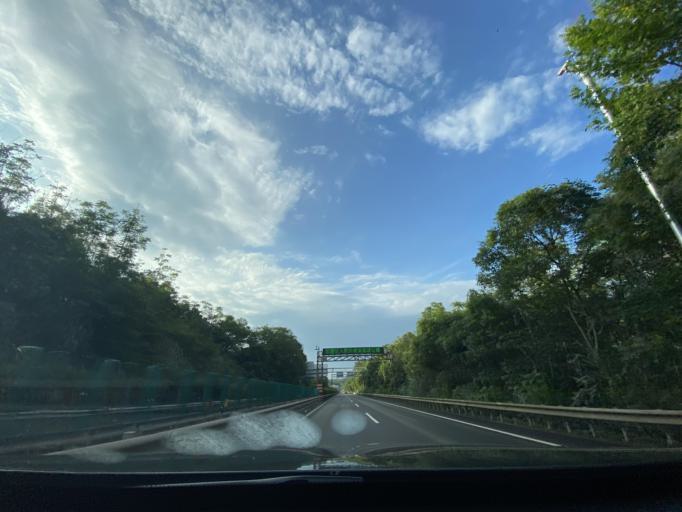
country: CN
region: Sichuan
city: Jiancheng
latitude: 30.3723
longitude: 104.5189
